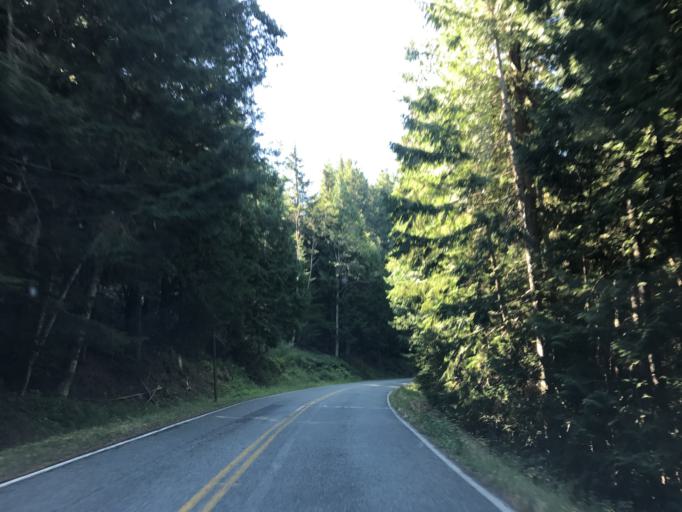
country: US
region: Washington
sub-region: King County
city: Enumclaw
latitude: 46.9150
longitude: -121.5362
